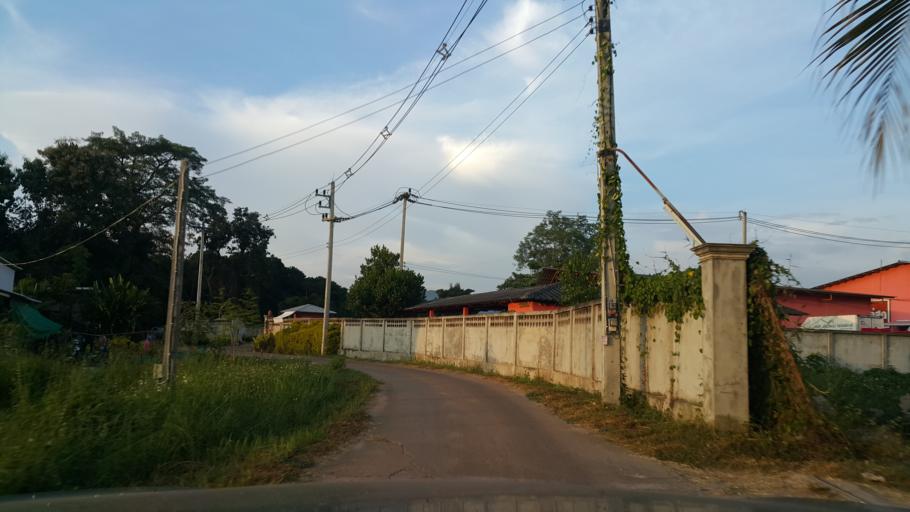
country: TH
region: Chiang Mai
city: San Sai
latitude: 18.8915
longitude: 99.0855
